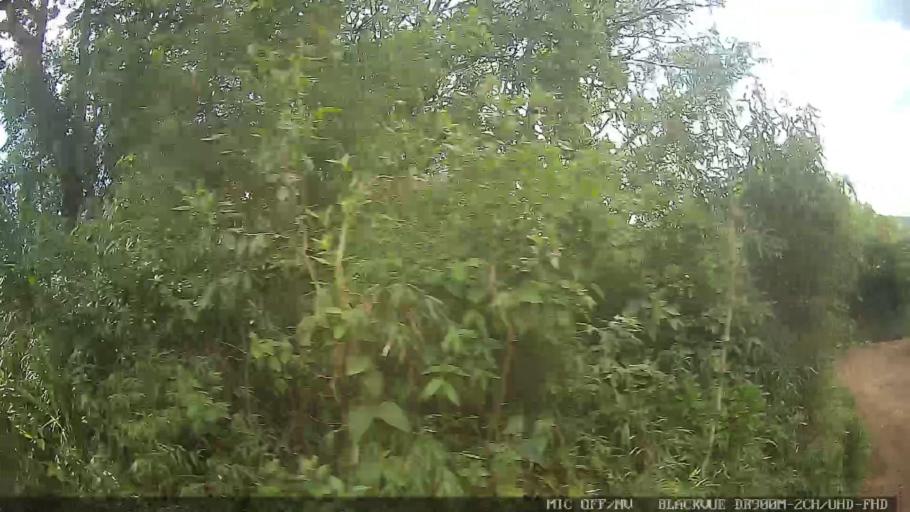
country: BR
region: Sao Paulo
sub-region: Atibaia
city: Atibaia
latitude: -23.1699
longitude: -46.5275
